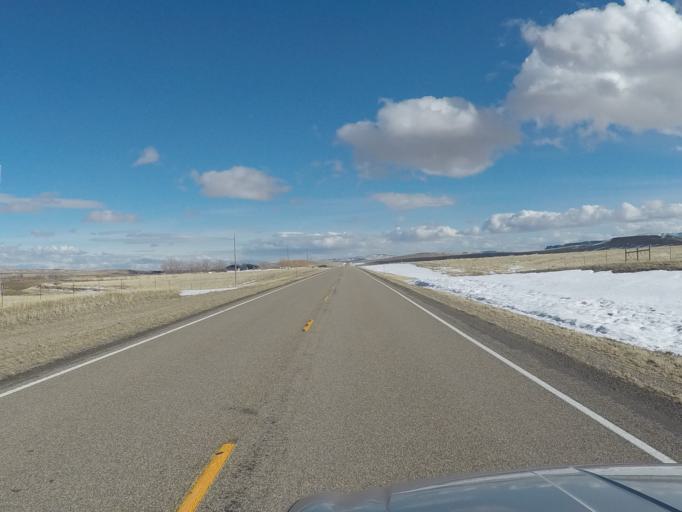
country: US
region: Montana
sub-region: Meagher County
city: White Sulphur Springs
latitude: 46.5297
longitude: -110.4232
